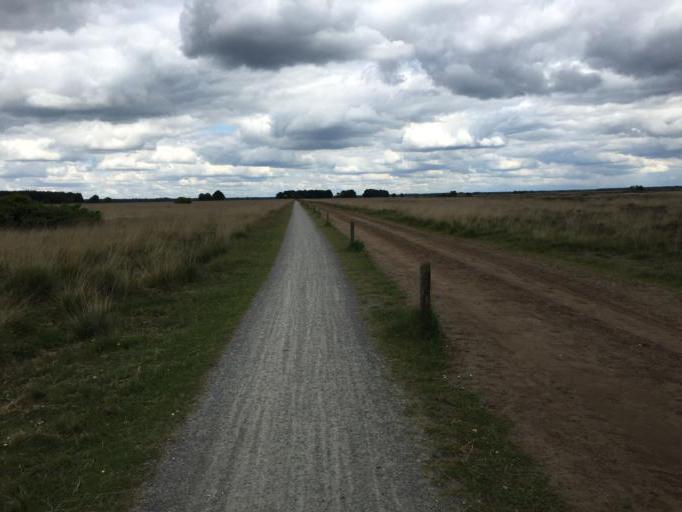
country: NL
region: Drenthe
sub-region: Gemeente De Wolden
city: Ruinen
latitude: 52.7865
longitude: 6.3802
